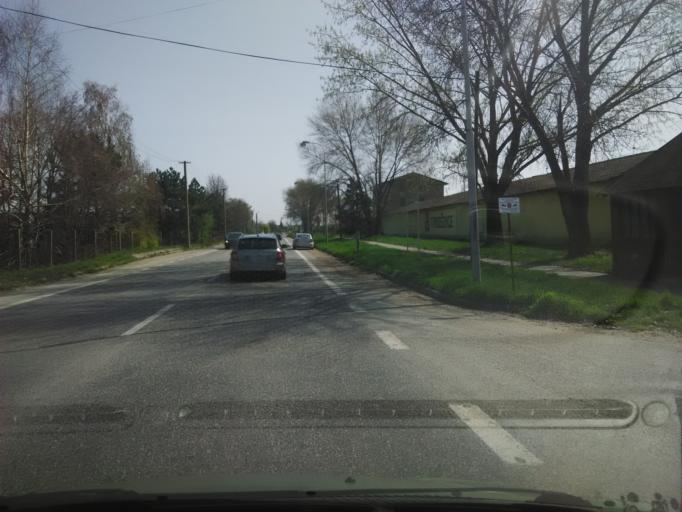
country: SK
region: Nitriansky
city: Surany
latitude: 48.1064
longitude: 18.0532
